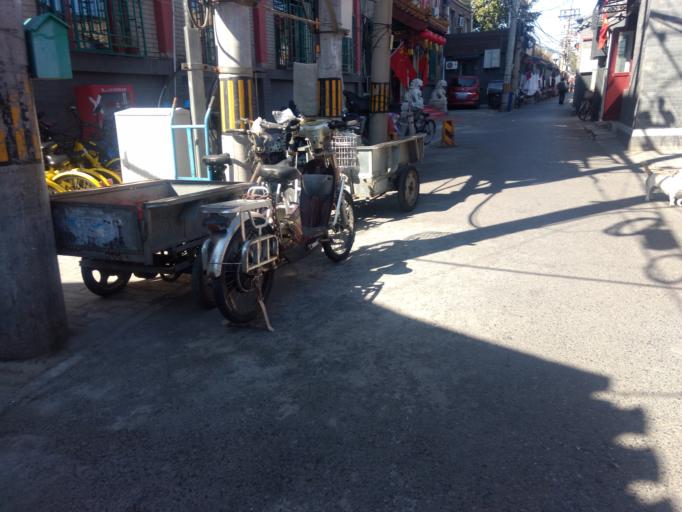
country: CN
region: Beijing
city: Beijing
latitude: 39.8904
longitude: 116.3836
